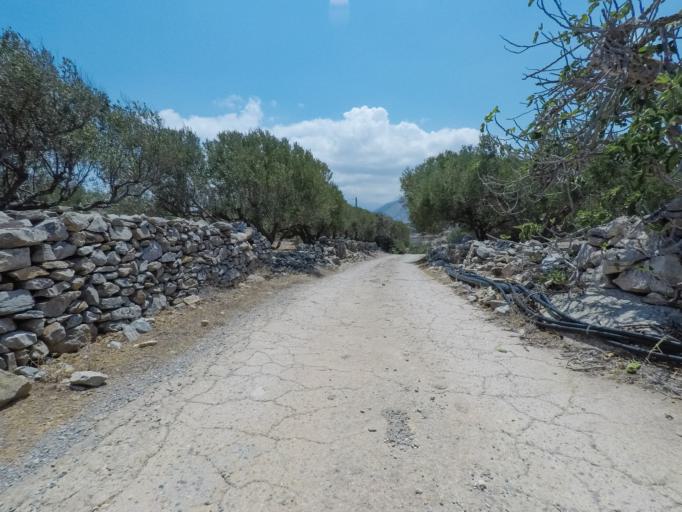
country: GR
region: Crete
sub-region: Nomos Lasithiou
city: Elounda
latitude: 35.3204
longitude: 25.7506
